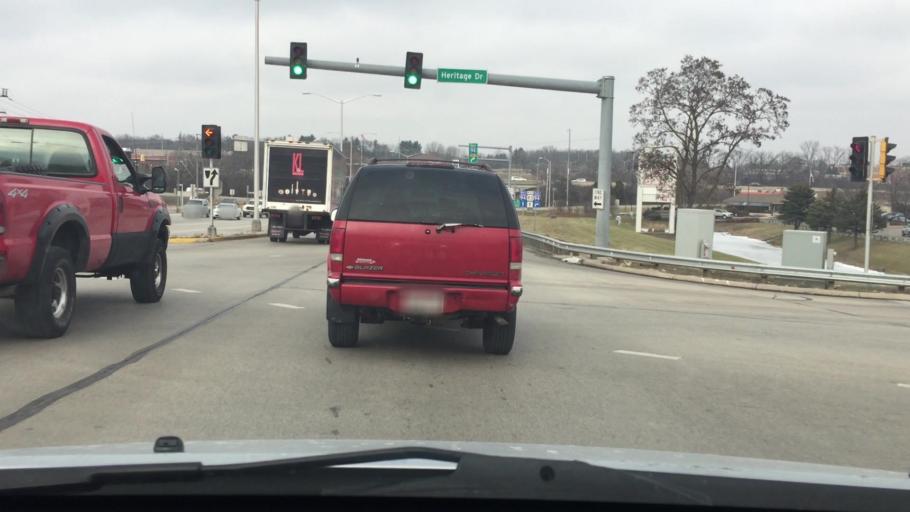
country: US
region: Wisconsin
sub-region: Waukesha County
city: Delafield
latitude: 43.0490
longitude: -88.3740
